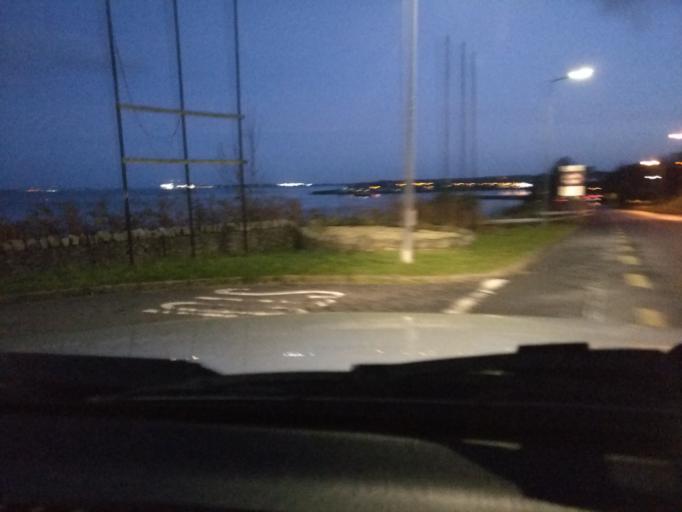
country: IE
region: Leinster
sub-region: Lu
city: Carlingford
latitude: 54.0475
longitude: -6.1906
